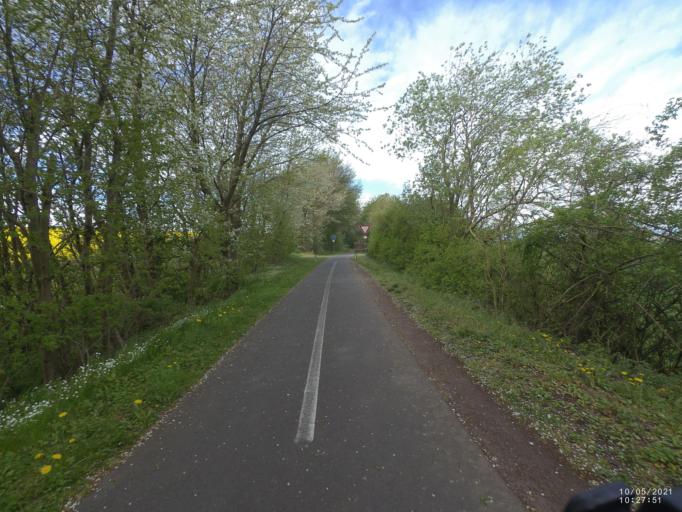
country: DE
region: Rheinland-Pfalz
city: Ochtendung
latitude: 50.3387
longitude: 7.3868
